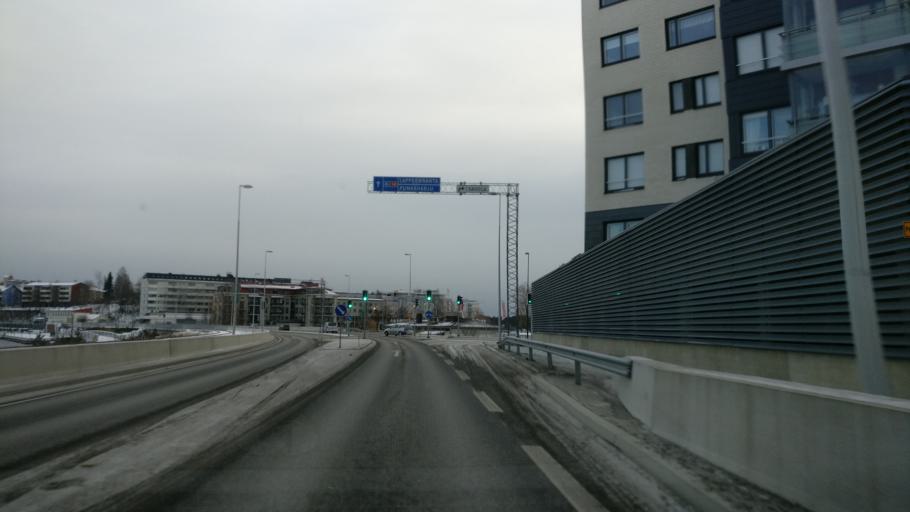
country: FI
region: Southern Savonia
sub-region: Savonlinna
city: Savonlinna
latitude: 61.8708
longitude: 28.8825
